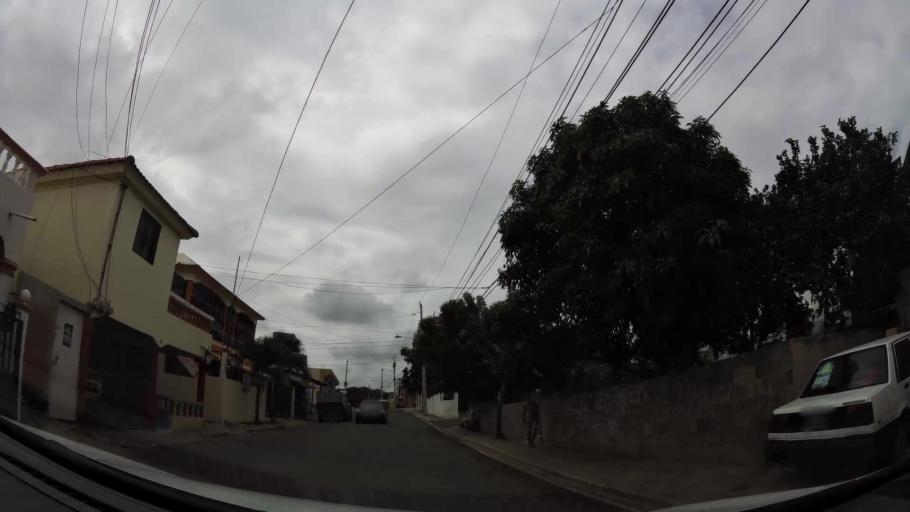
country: DO
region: Santiago
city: Santiago de los Caballeros
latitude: 19.4280
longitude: -70.6628
